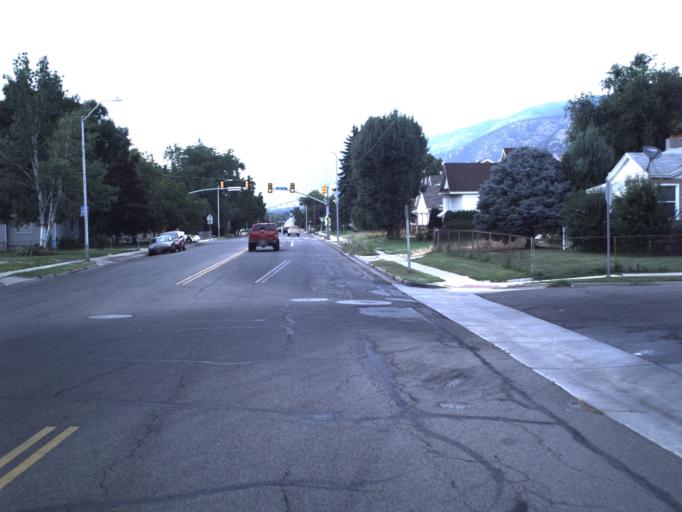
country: US
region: Utah
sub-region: Davis County
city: Bountiful
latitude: 40.8985
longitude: -111.8790
